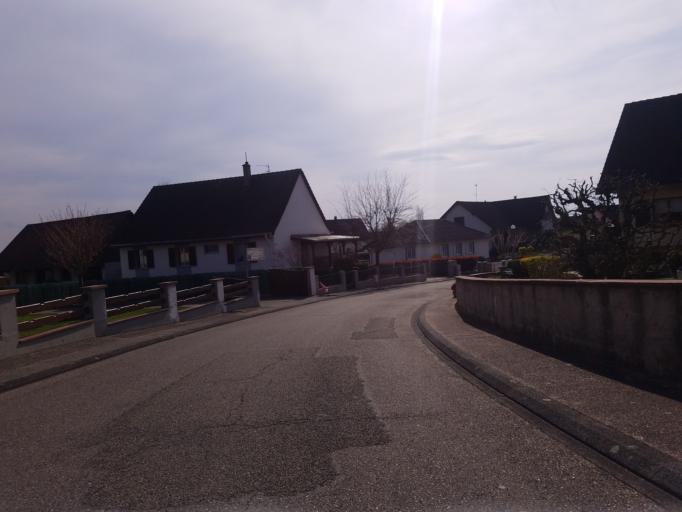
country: FR
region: Alsace
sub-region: Departement du Bas-Rhin
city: Betschdorf
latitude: 48.8975
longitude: 7.9160
